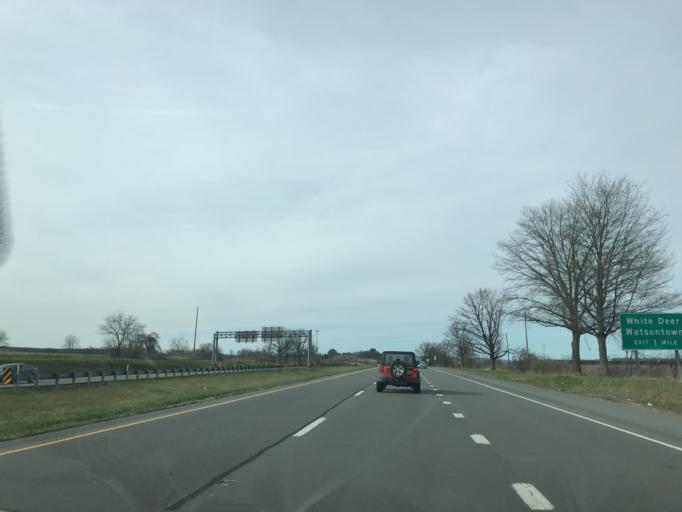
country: US
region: Pennsylvania
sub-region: Union County
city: New Columbia
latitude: 41.0563
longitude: -76.8716
